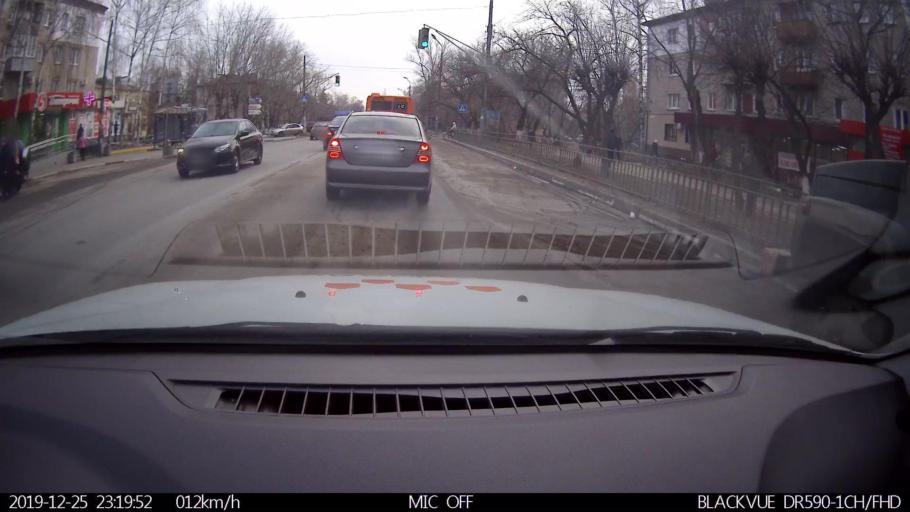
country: RU
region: Nizjnij Novgorod
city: Gorbatovka
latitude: 56.3541
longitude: 43.8319
